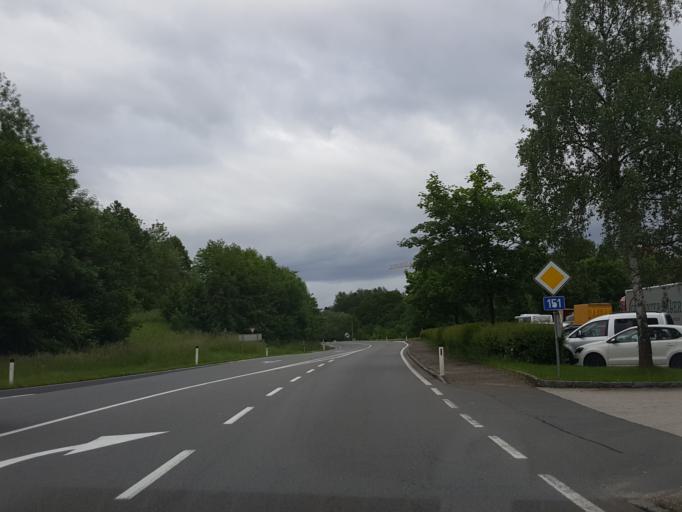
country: AT
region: Upper Austria
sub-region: Politischer Bezirk Vocklabruck
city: Seewalchen
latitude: 47.9495
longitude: 13.5975
